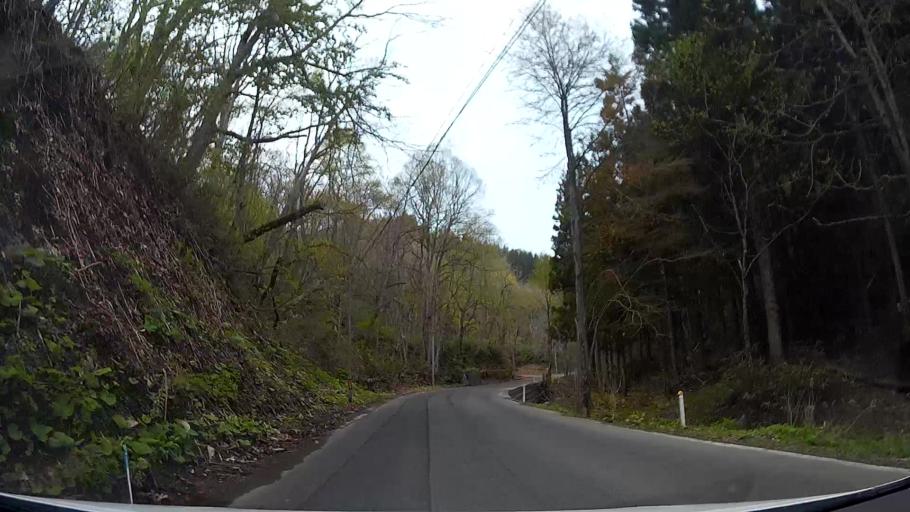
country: JP
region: Akita
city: Hanawa
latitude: 40.3812
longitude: 140.8896
